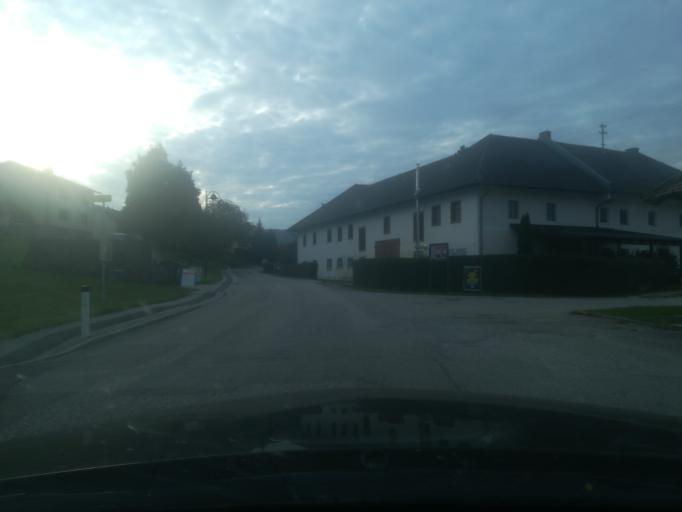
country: AT
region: Upper Austria
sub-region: Wels-Land
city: Buchkirchen
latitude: 48.2580
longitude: 14.0412
